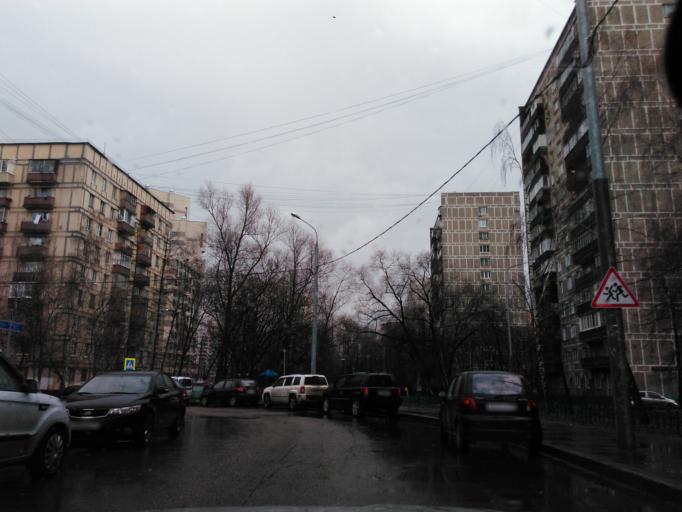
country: RU
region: Moskovskaya
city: Levoberezhnaya
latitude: 55.8668
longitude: 37.4693
